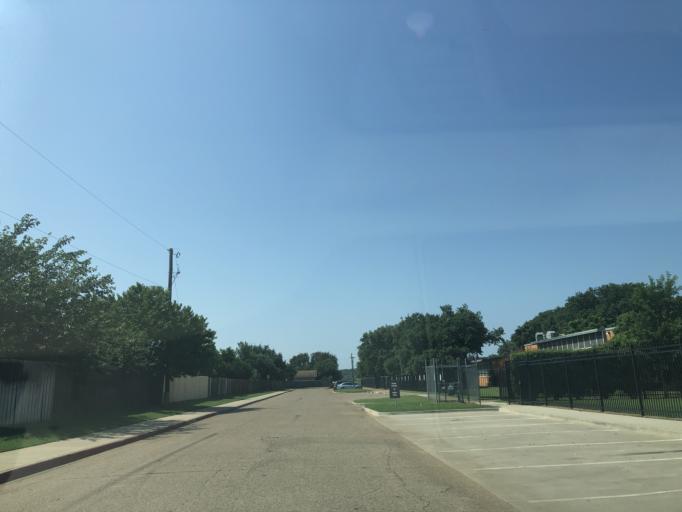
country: US
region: Texas
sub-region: Dallas County
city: Cockrell Hill
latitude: 32.7905
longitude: -96.8655
